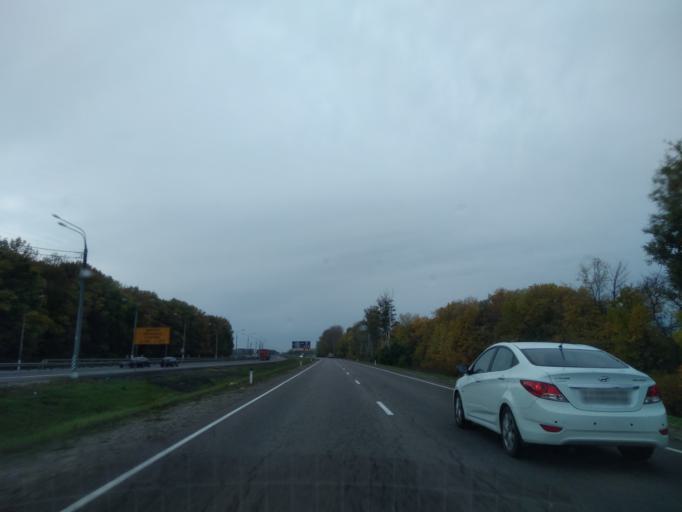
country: RU
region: Lipetsk
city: Zadonsk
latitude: 52.4403
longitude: 38.8050
